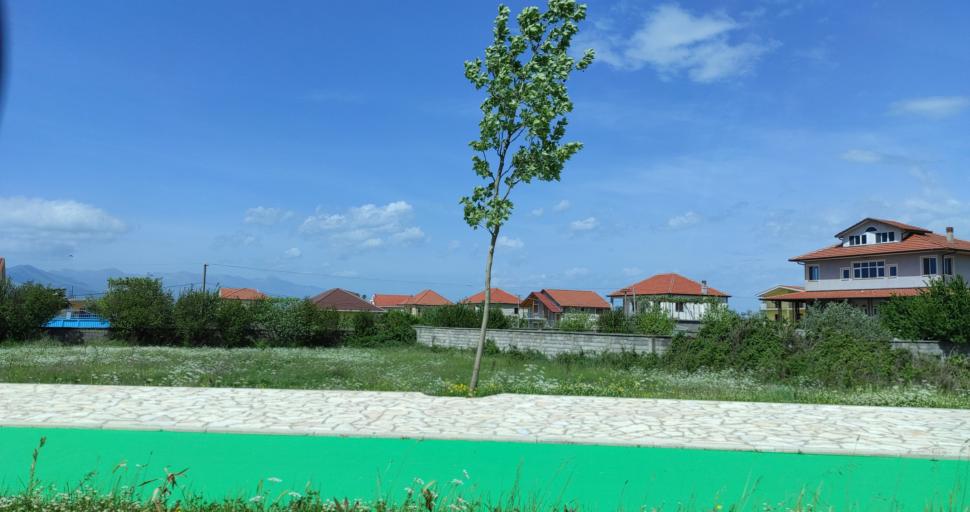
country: AL
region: Shkoder
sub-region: Rrethi i Shkodres
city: Shkoder
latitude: 42.0858
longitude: 19.5037
